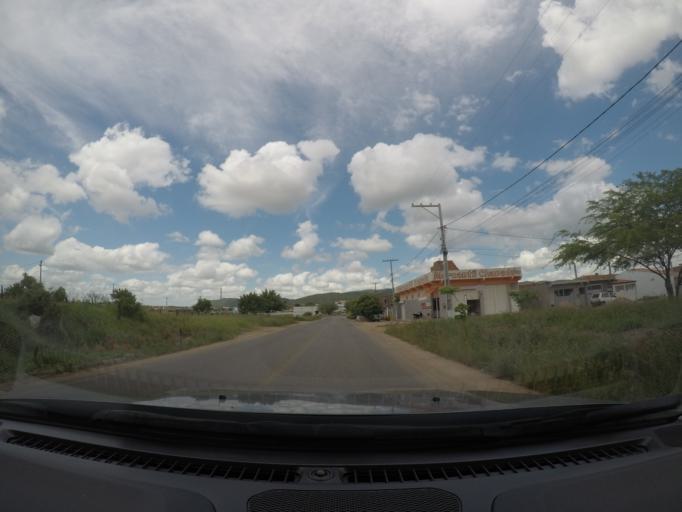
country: BR
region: Bahia
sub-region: Ipira
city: Ipira
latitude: -12.1649
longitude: -39.7485
